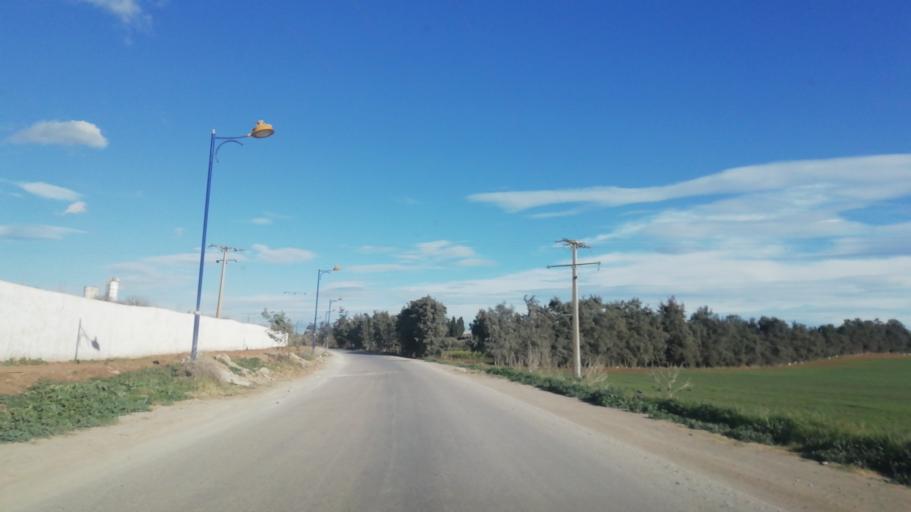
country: DZ
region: Oran
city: Sidi ech Chahmi
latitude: 35.6403
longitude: -0.5424
